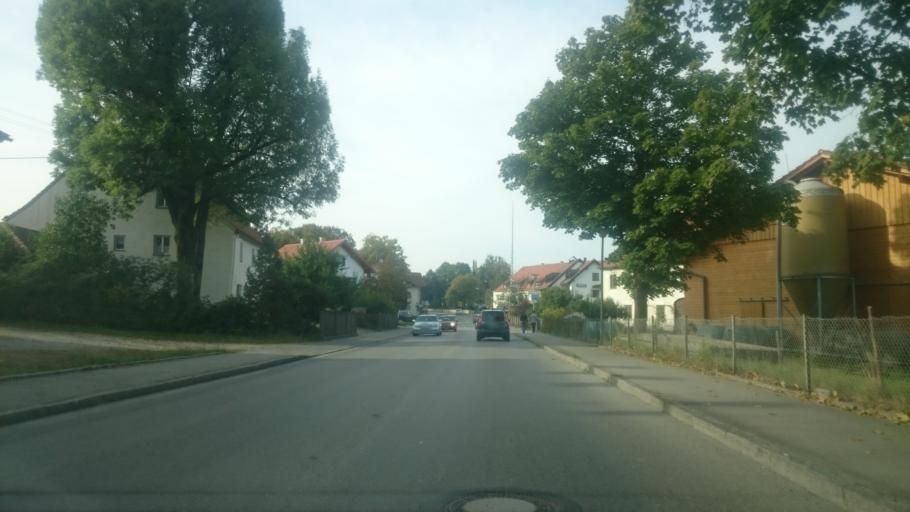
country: DE
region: Bavaria
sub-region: Upper Bavaria
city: Steingaden
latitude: 47.7029
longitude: 10.8610
